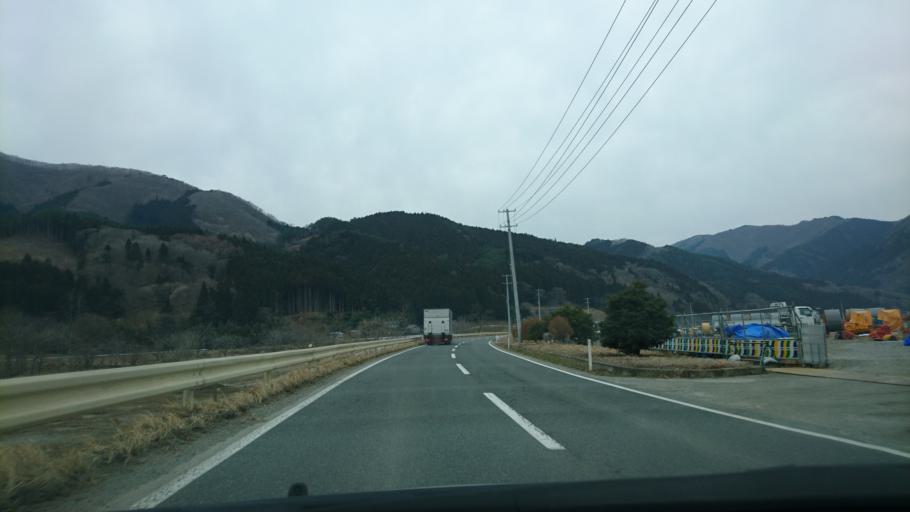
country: JP
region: Iwate
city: Ofunato
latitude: 39.0694
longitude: 141.5833
